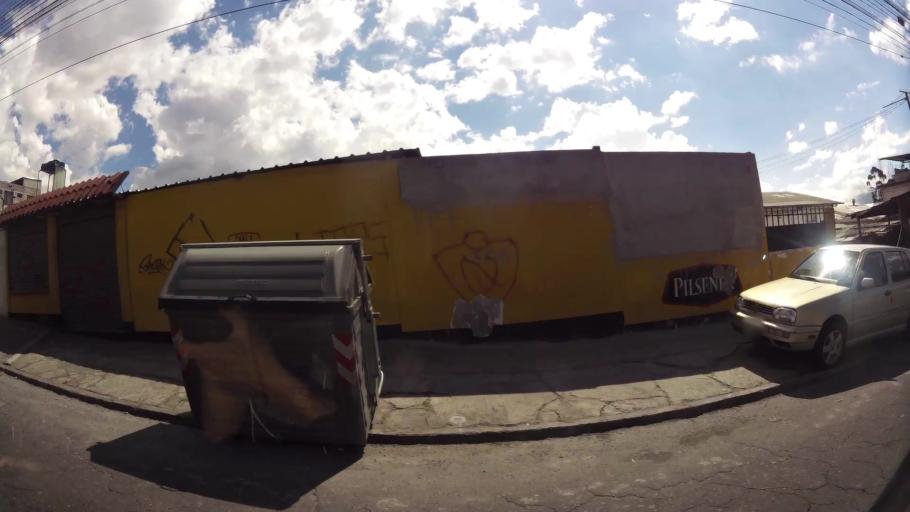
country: EC
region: Pichincha
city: Quito
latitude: -0.1129
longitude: -78.4745
